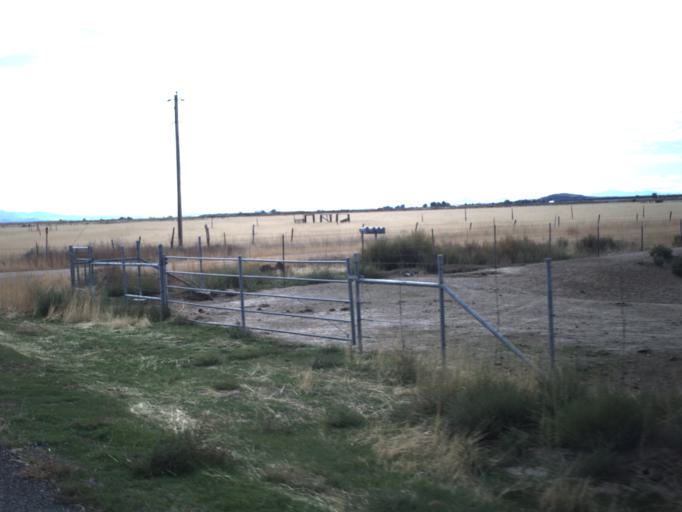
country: US
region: Utah
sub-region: Millard County
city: Fillmore
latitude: 39.0236
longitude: -112.4100
